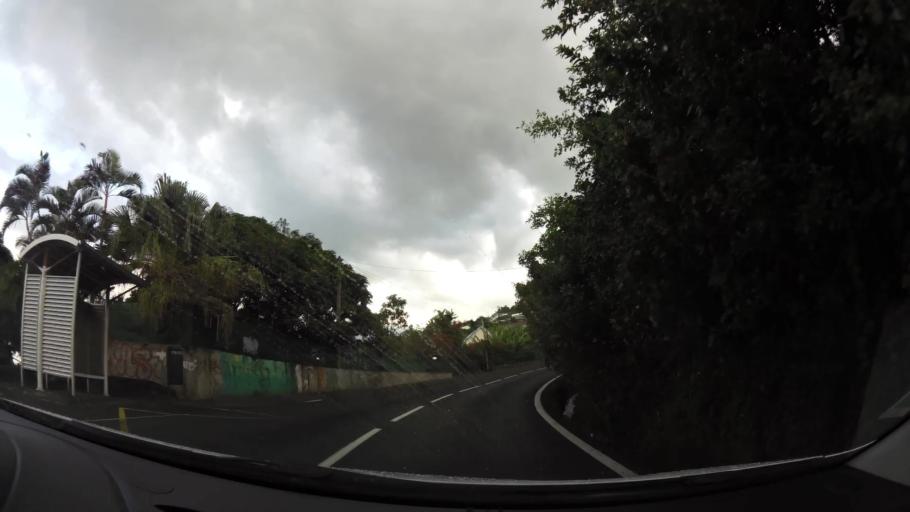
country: RE
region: Reunion
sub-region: Reunion
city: Saint-Denis
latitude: -20.9023
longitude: 55.4428
